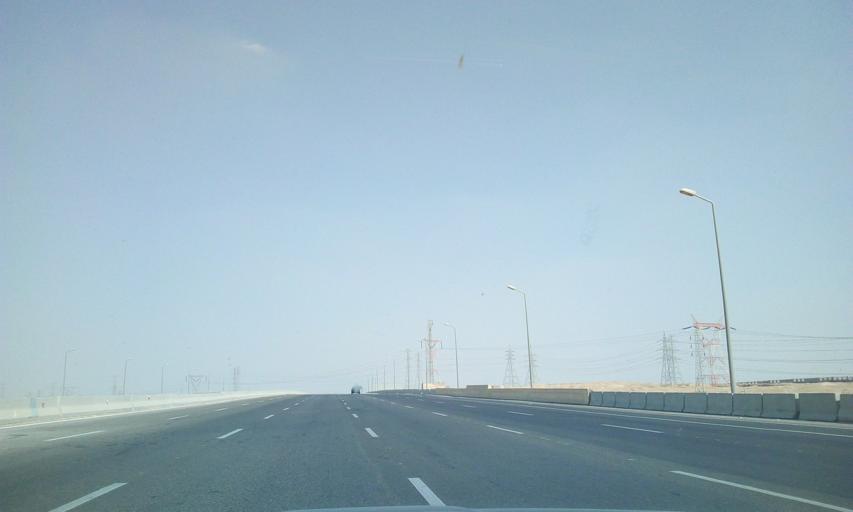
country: EG
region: Muhafazat al Qahirah
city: Halwan
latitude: 29.9065
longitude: 31.6769
